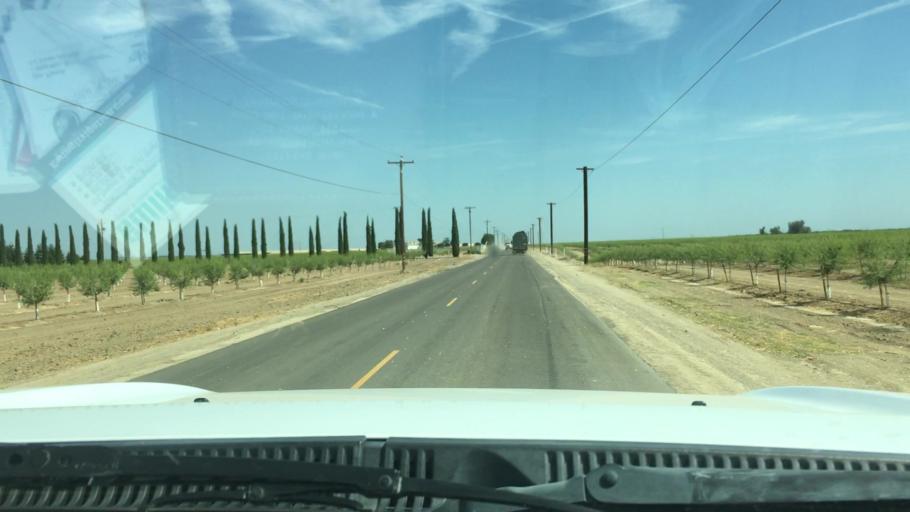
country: US
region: California
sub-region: Kern County
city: Shafter
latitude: 35.4573
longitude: -119.3681
